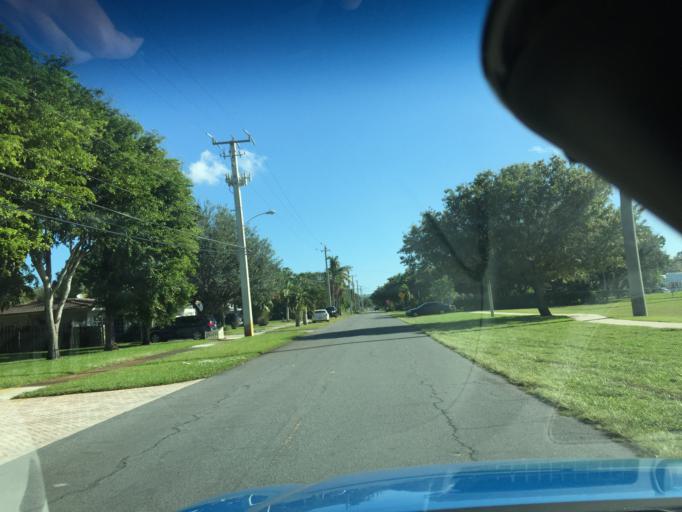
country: US
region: Florida
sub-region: Broward County
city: Pompano Beach
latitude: 26.2371
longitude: -80.1161
